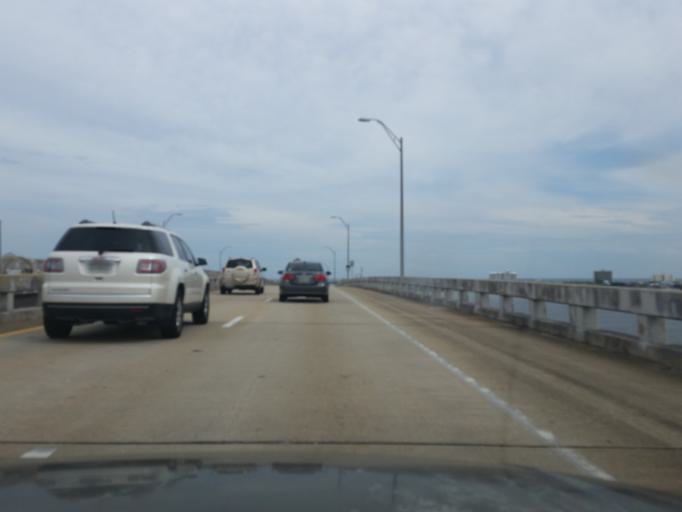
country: US
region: Florida
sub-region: Santa Rosa County
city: Gulf Breeze
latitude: 30.3486
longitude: -87.1540
